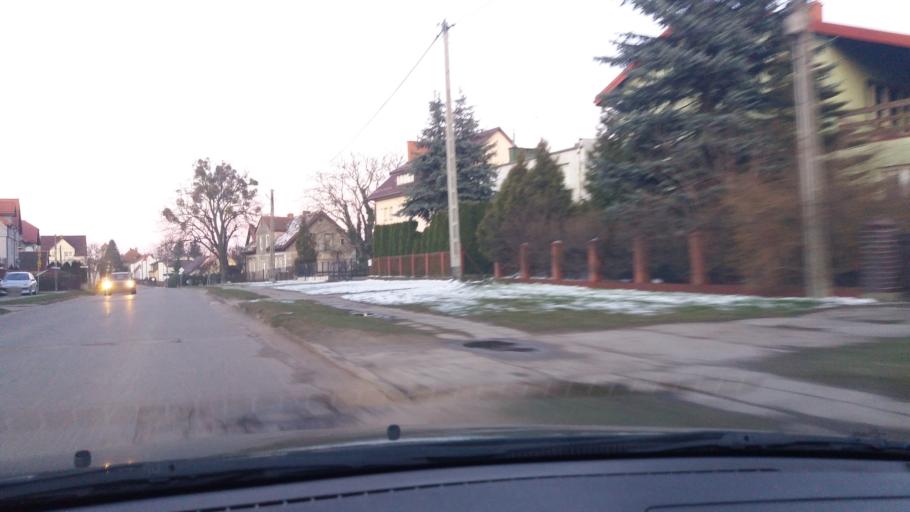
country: PL
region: Warmian-Masurian Voivodeship
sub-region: Powiat szczycienski
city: Szczytno
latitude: 53.5593
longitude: 20.9805
